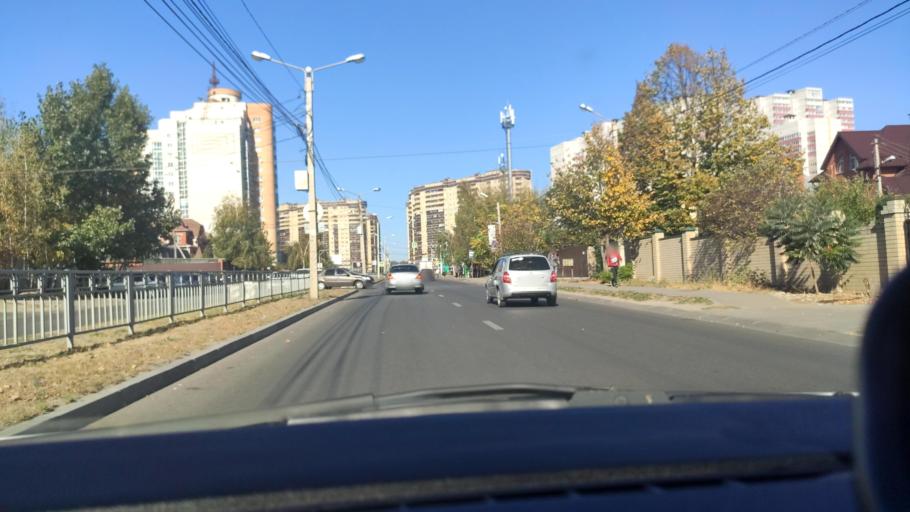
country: RU
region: Voronezj
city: Voronezh
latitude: 51.7096
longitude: 39.1953
